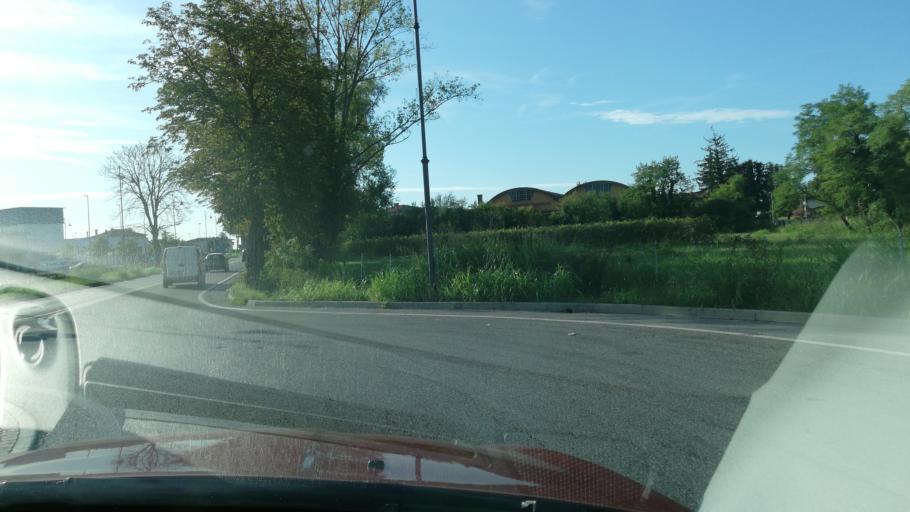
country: IT
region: Veneto
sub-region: Provincia di Venezia
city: Santo Stino di Livenza
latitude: 45.7234
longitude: 12.6975
